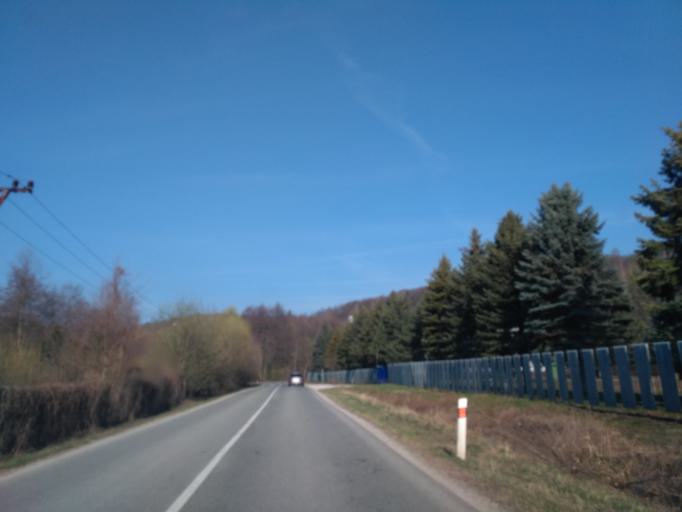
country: SK
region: Kosicky
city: Medzev
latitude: 48.7090
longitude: 20.8769
